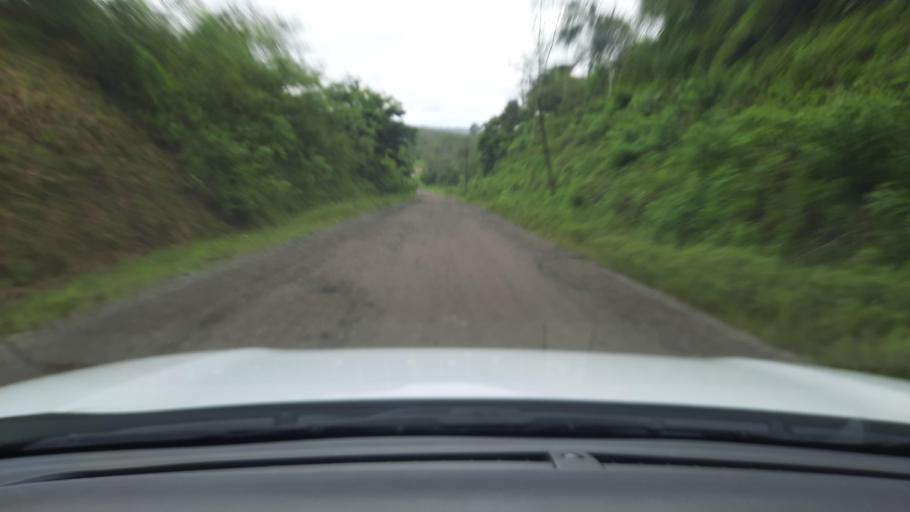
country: CR
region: Alajuela
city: San Jose
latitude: 10.9995
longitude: -85.2858
